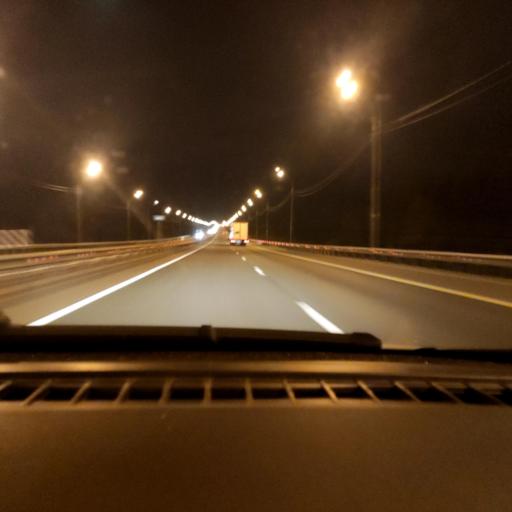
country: RU
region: Lipetsk
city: Khlevnoye
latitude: 52.2040
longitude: 39.1613
